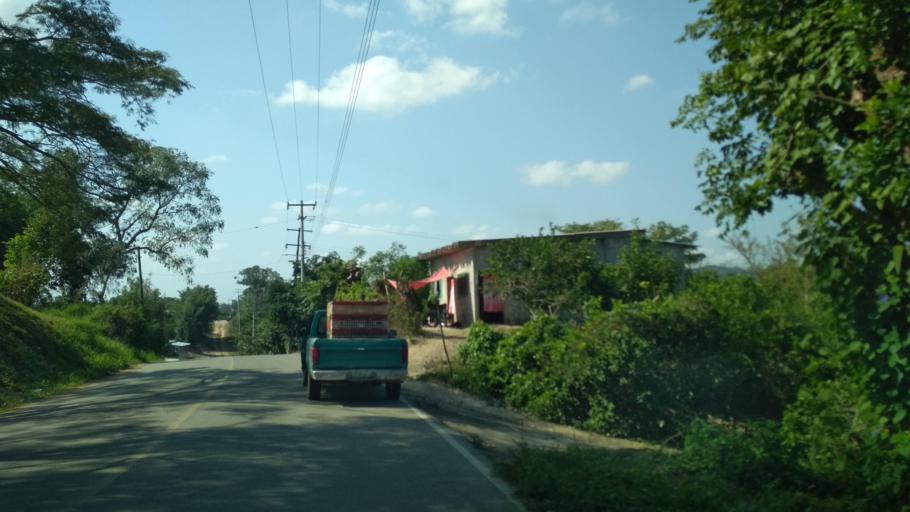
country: MX
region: Puebla
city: San Jose Acateno
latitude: 20.1912
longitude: -97.1532
